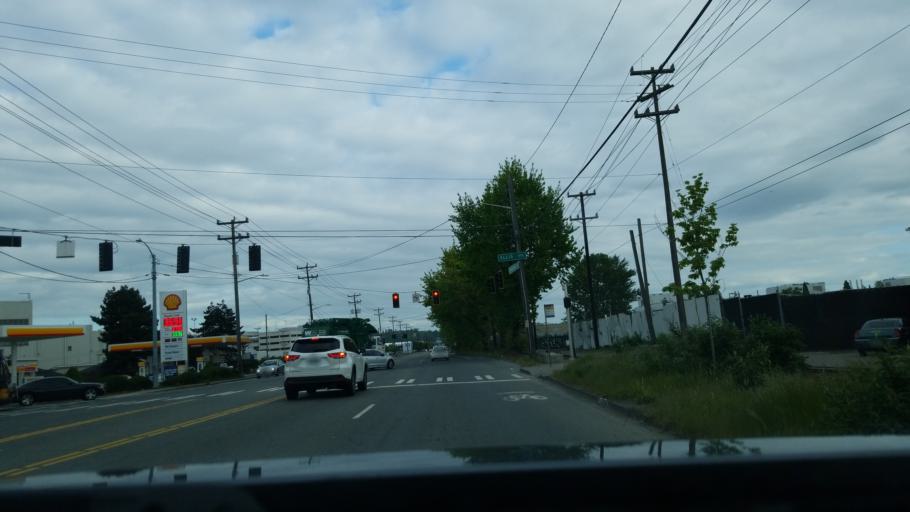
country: US
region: Washington
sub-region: King County
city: White Center
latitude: 47.5389
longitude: -122.3212
